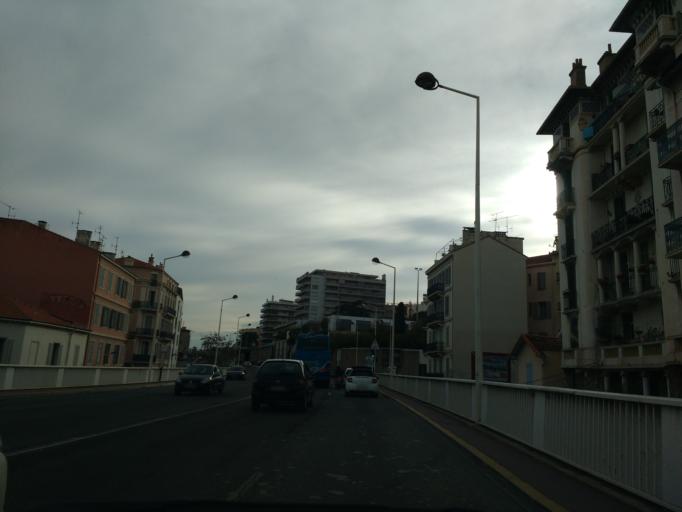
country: FR
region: Provence-Alpes-Cote d'Azur
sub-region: Departement des Alpes-Maritimes
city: Cannes
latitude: 43.5530
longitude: 7.0117
